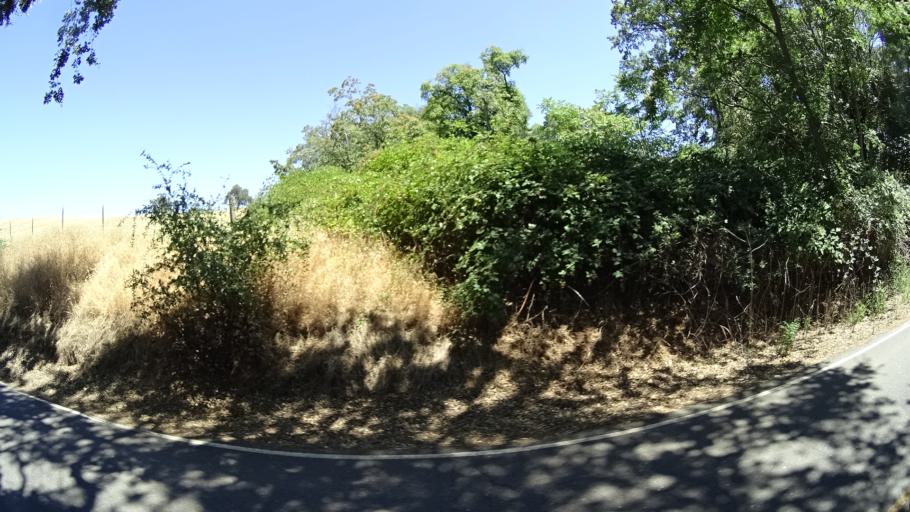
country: US
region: California
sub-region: Calaveras County
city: Murphys
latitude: 38.1184
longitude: -120.5104
